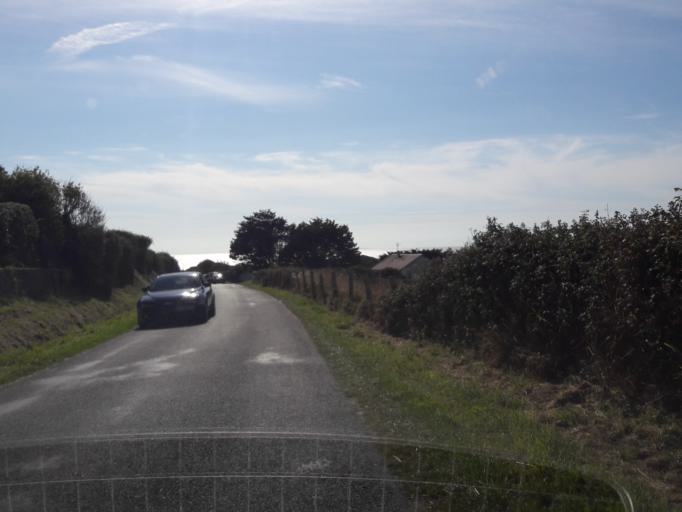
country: FR
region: Lower Normandy
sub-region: Departement de la Manche
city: Surtainville
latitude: 49.4793
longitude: -1.8396
